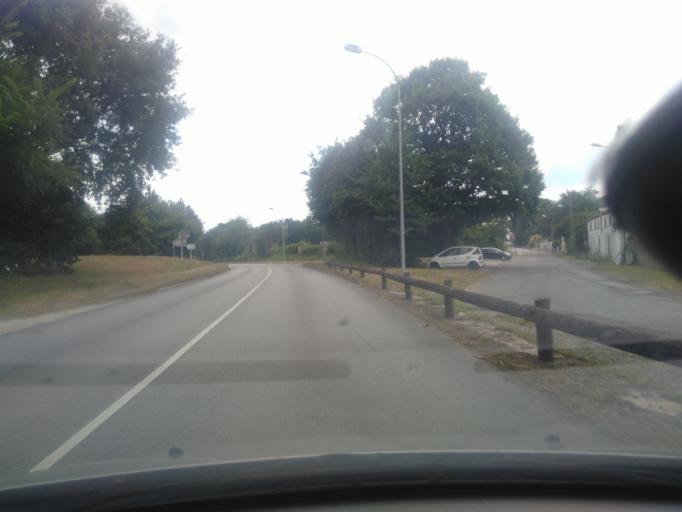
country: FR
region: Pays de la Loire
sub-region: Departement de la Vendee
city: La Roche-sur-Yon
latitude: 46.6917
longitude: -1.4402
